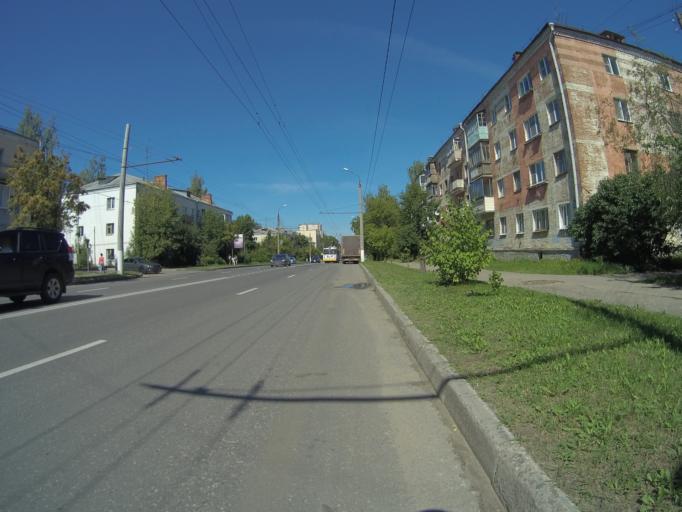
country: RU
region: Vladimir
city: Vladimir
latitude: 56.1249
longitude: 40.3617
